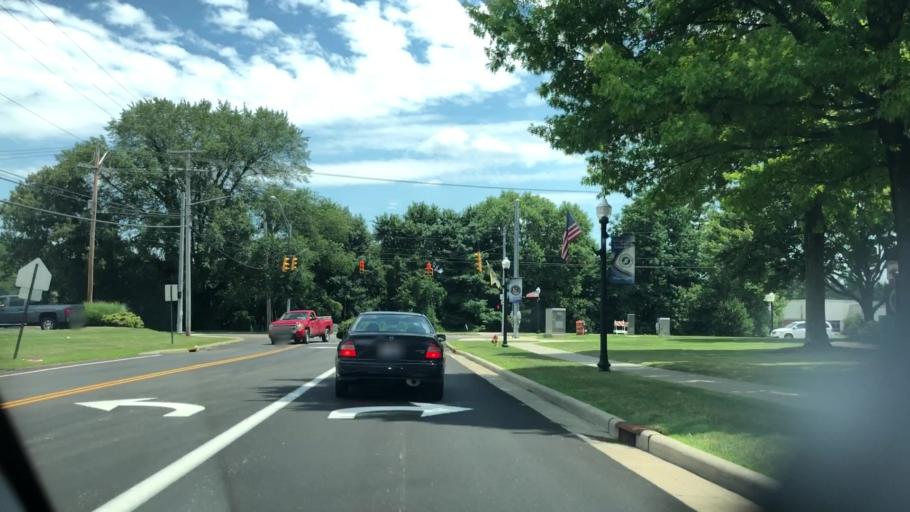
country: US
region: Ohio
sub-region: Summit County
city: Greensburg
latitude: 40.8653
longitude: -81.4851
